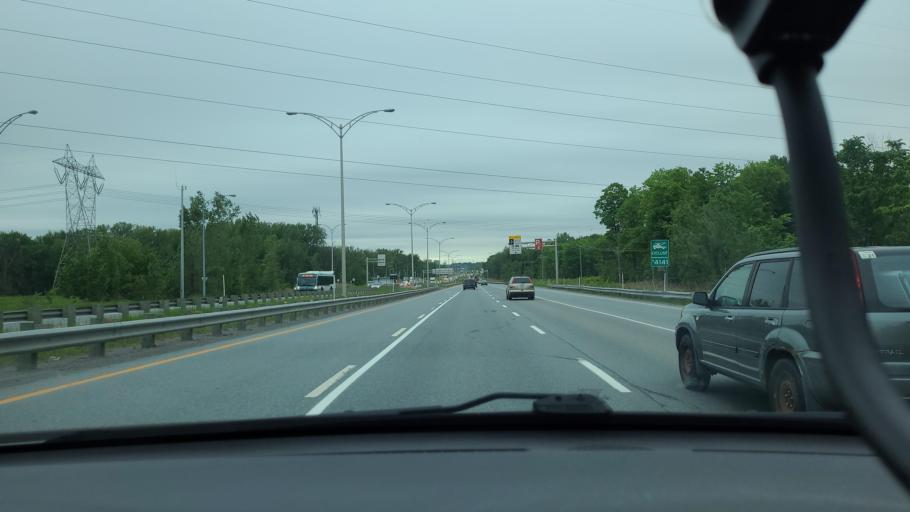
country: CA
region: Quebec
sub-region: Lanaudiere
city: Terrebonne
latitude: 45.6701
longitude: -73.6501
